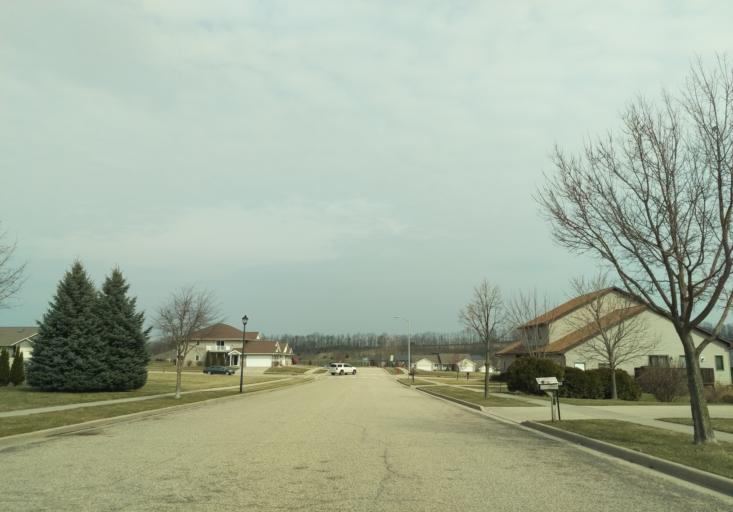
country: US
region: Wisconsin
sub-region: Columbia County
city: Lodi
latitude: 43.3087
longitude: -89.5444
